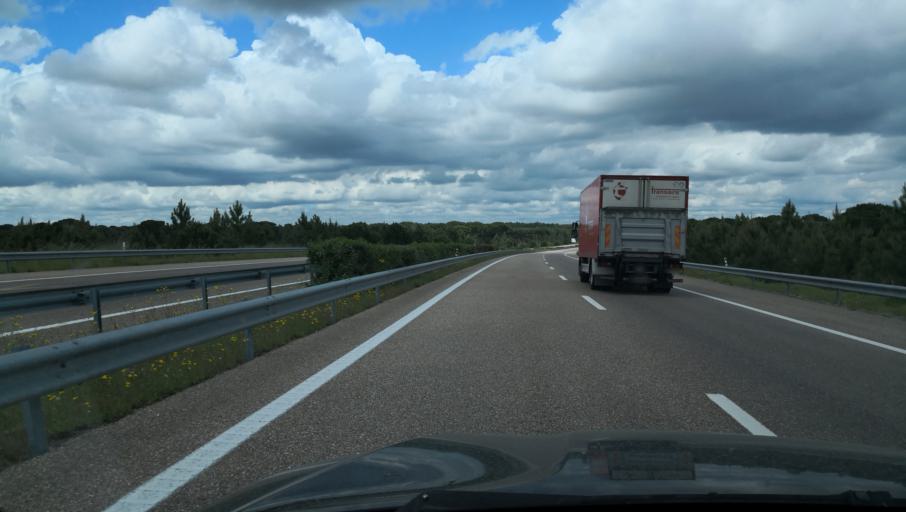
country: PT
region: Evora
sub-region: Vendas Novas
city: Vendas Novas
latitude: 38.6488
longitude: -8.6657
